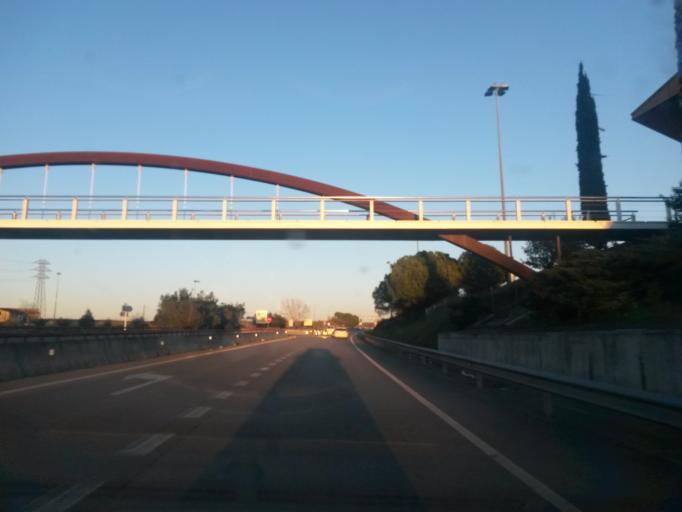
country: ES
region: Catalonia
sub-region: Provincia de Girona
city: Macanet de la Selva
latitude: 41.7841
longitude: 2.7470
